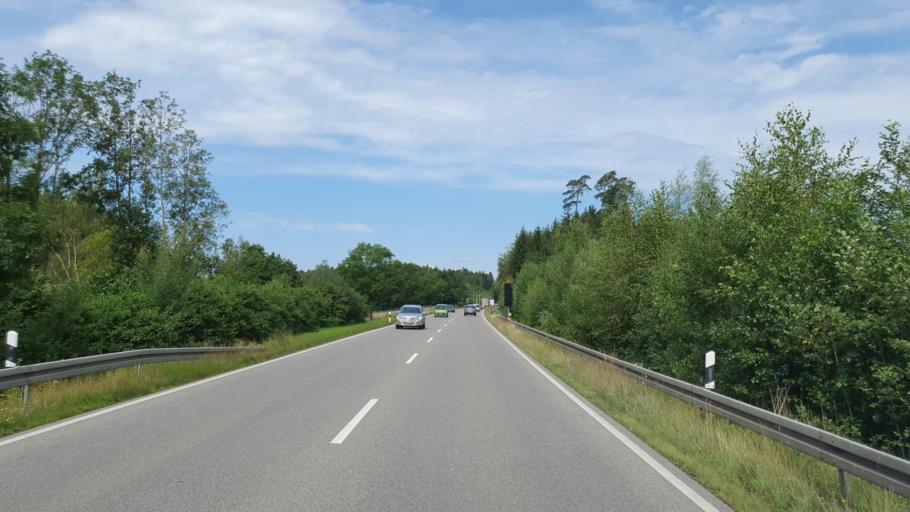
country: DE
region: Bavaria
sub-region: Swabia
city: Bodolz
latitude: 47.5881
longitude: 9.6511
